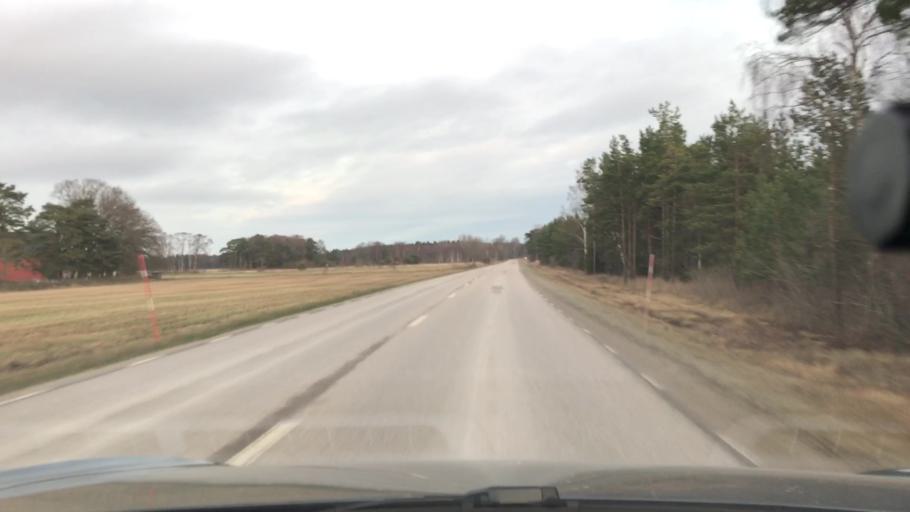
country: SE
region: Gotland
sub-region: Gotland
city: Slite
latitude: 57.7178
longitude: 18.5543
